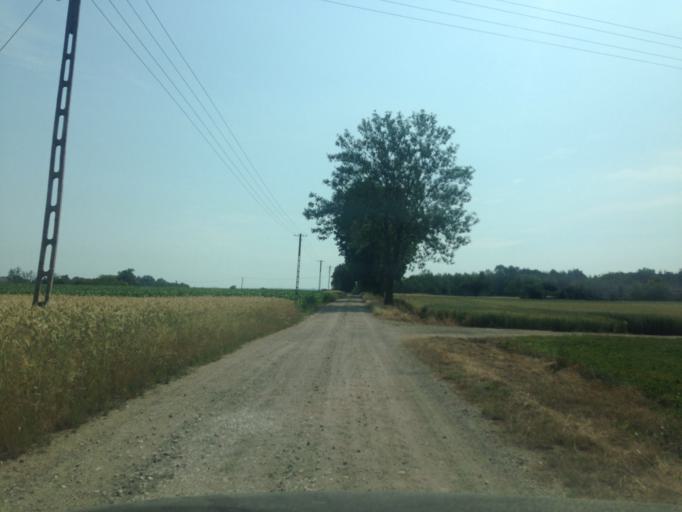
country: PL
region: Kujawsko-Pomorskie
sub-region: Powiat rypinski
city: Wapielsk
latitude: 53.2029
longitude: 19.2432
